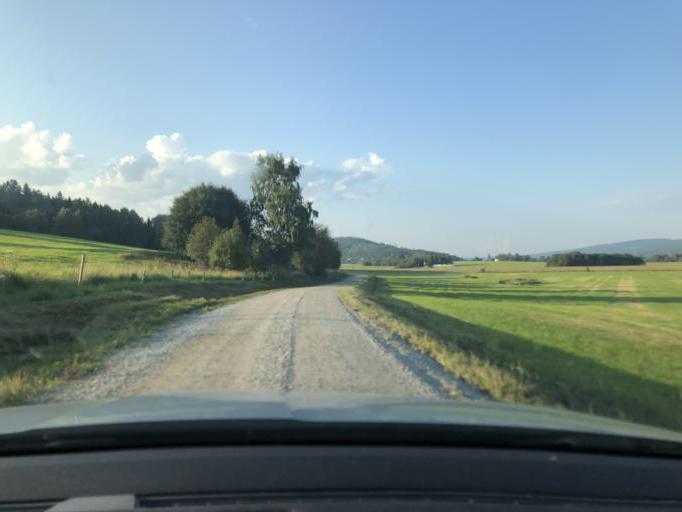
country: SE
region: Vaesternorrland
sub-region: Kramfors Kommun
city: Bollstabruk
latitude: 63.0663
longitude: 17.7346
